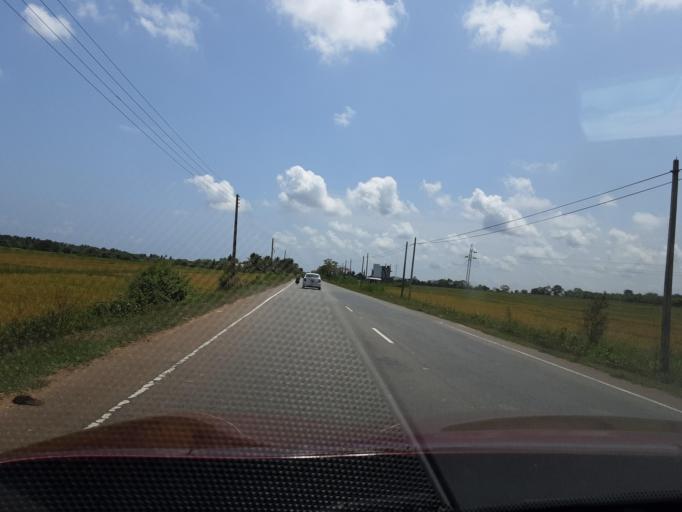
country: LK
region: Southern
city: Tangalla
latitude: 6.2189
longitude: 81.2143
